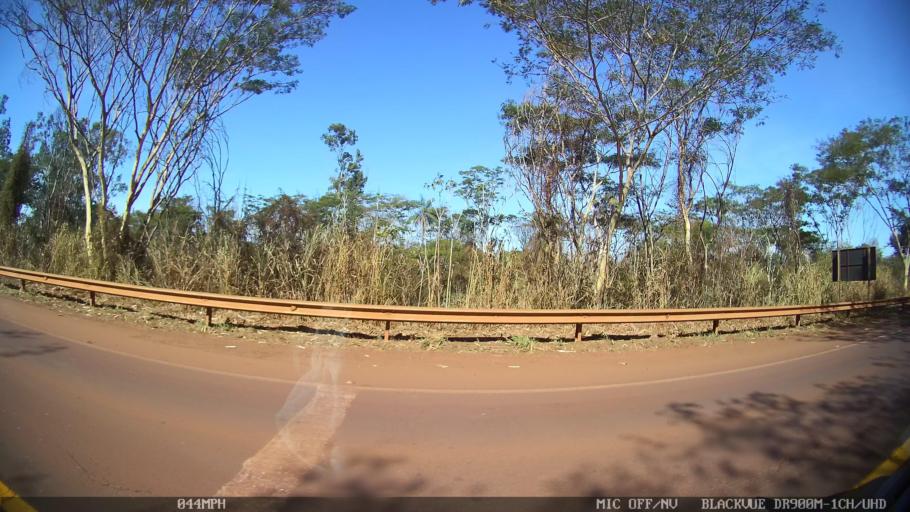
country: BR
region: Sao Paulo
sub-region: Barretos
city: Barretos
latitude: -20.4536
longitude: -48.4578
